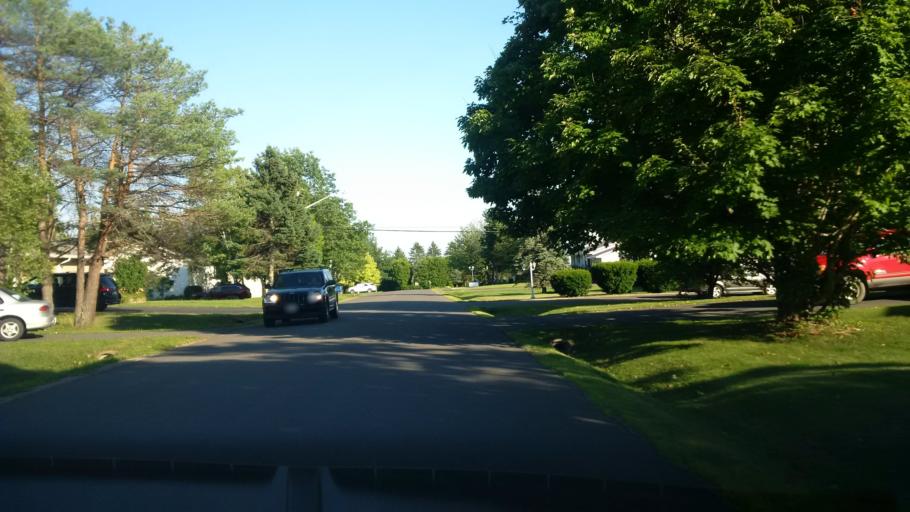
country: CA
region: New Brunswick
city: Fredericton
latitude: 45.8966
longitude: -66.6857
